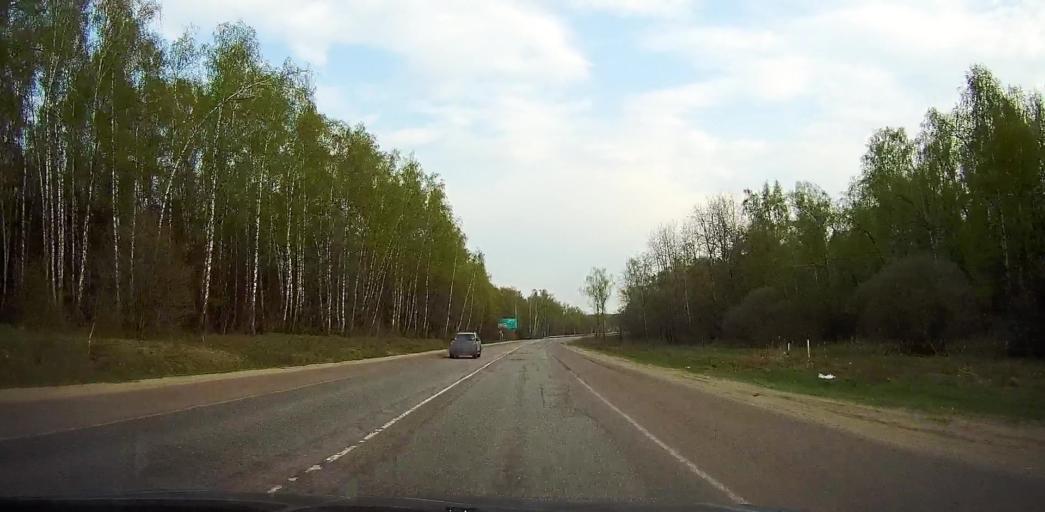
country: RU
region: Moskovskaya
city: Petrovskaya
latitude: 55.5296
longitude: 37.7836
